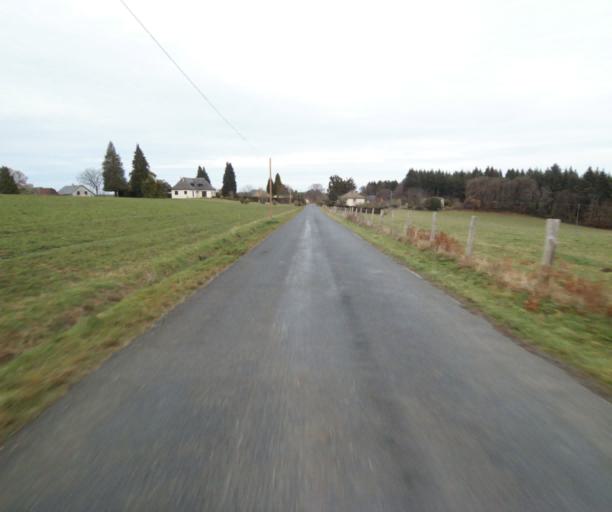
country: FR
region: Limousin
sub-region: Departement de la Correze
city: Chameyrat
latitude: 45.2367
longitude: 1.6617
